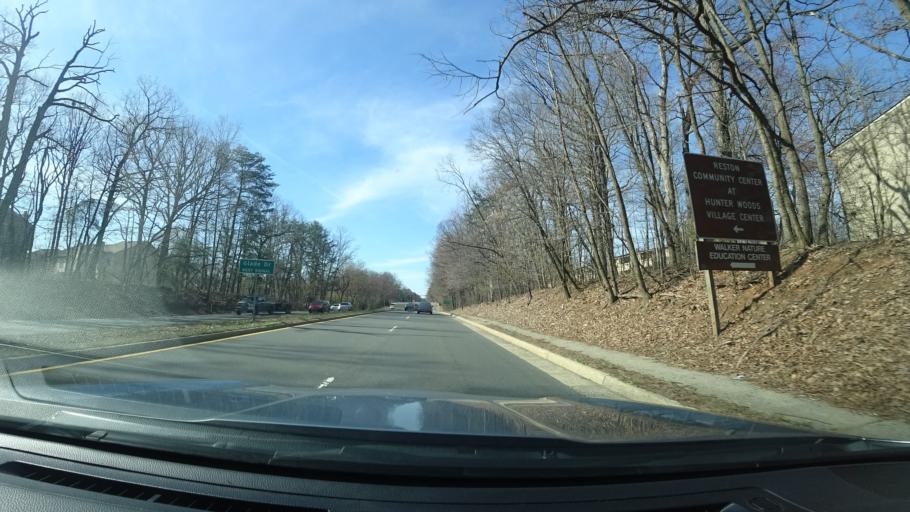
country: US
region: Virginia
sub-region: Fairfax County
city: Herndon
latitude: 38.9377
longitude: -77.3652
